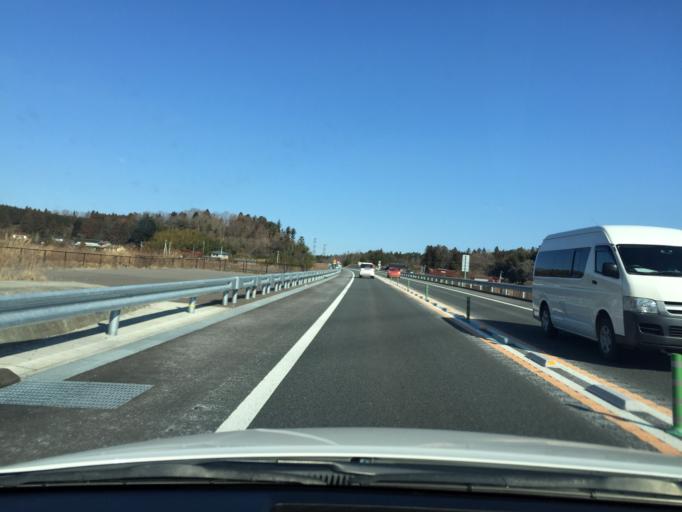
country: JP
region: Fukushima
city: Namie
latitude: 37.5153
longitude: 140.9439
